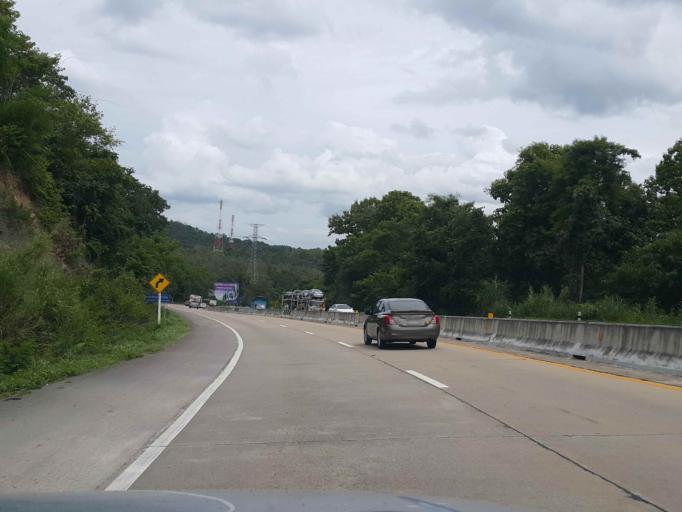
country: TH
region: Lampang
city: Hang Chat
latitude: 18.3602
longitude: 99.2386
